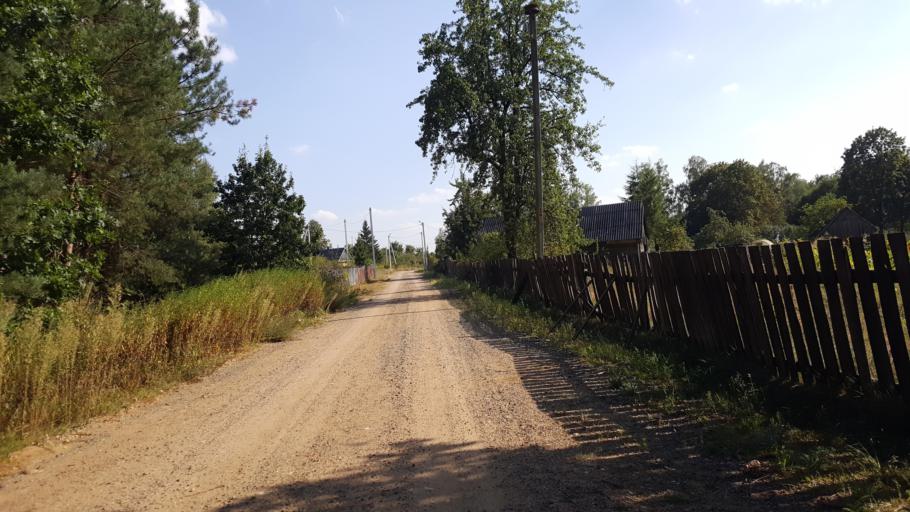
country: BY
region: Brest
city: Kamyanyuki
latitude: 52.5639
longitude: 23.6314
